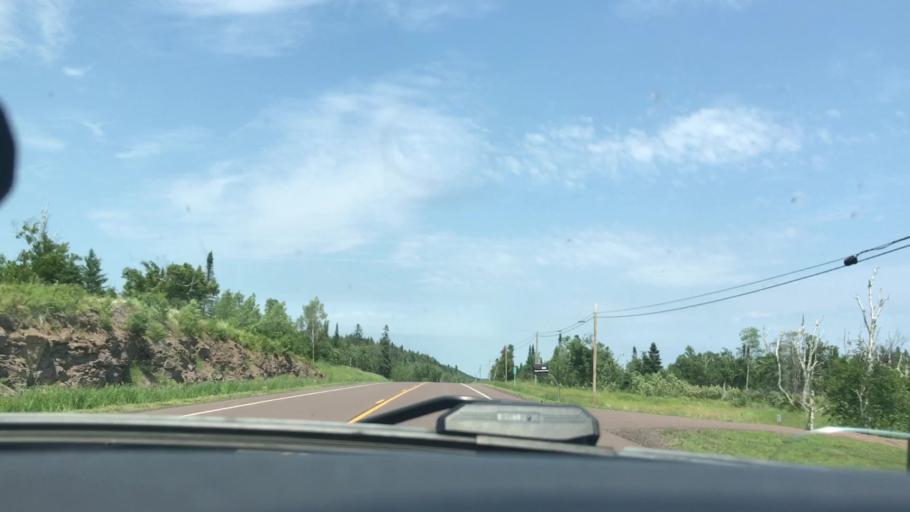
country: US
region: Minnesota
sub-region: Lake County
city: Silver Bay
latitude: 47.4304
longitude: -91.0867
